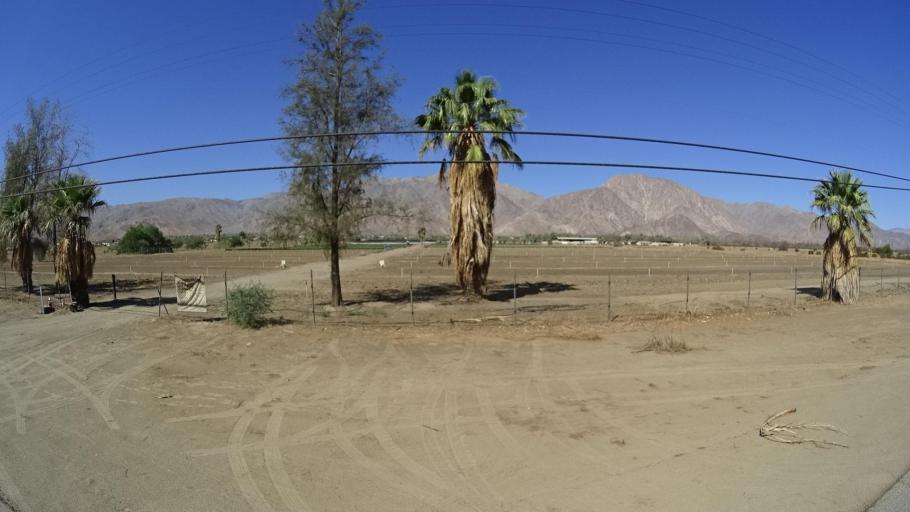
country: US
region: California
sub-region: San Diego County
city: Borrego Springs
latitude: 33.2679
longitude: -116.3661
